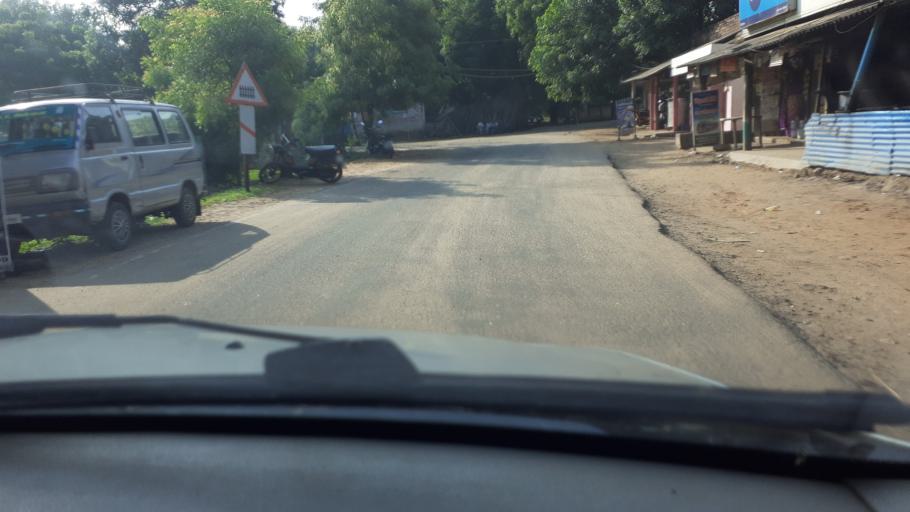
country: IN
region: Tamil Nadu
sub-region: Thoothukkudi
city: Eral
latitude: 8.5786
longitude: 78.0224
